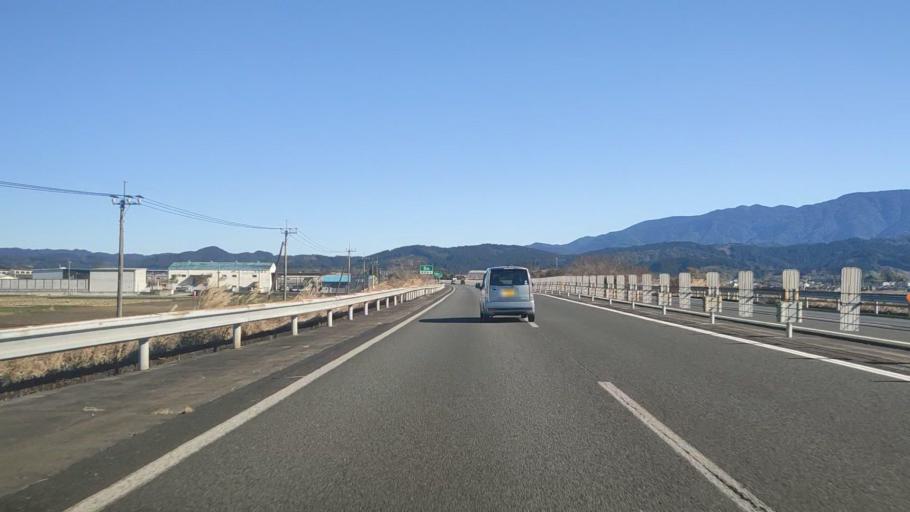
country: JP
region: Miyazaki
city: Miyakonojo
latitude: 31.7835
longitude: 131.1391
